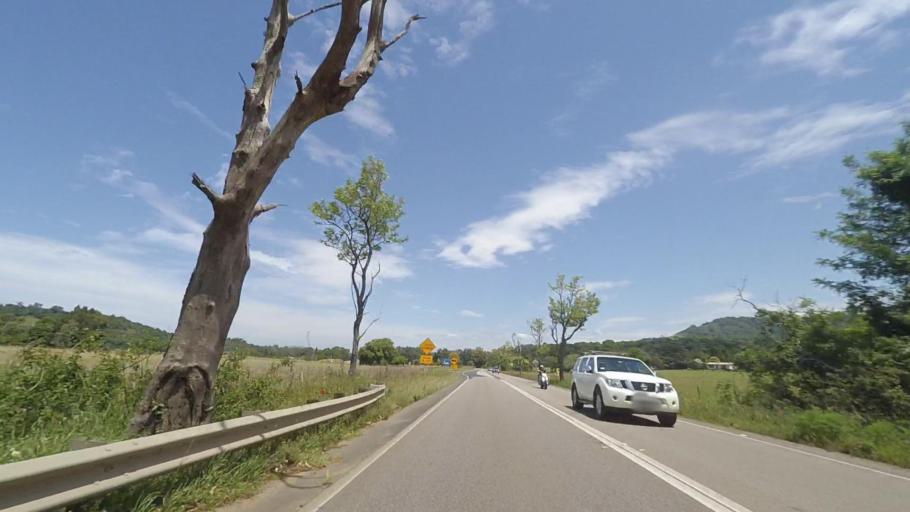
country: AU
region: New South Wales
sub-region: Kiama
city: Gerringong
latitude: -34.7412
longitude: 150.7628
